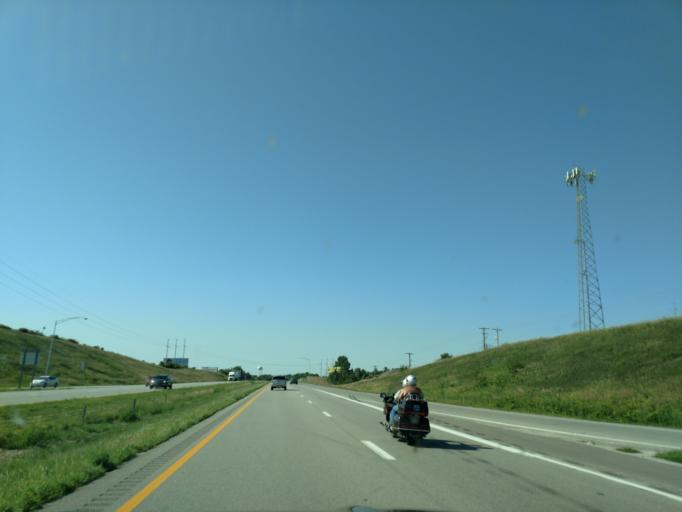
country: US
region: Missouri
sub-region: Buchanan County
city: Saint Joseph
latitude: 39.7783
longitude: -94.7938
